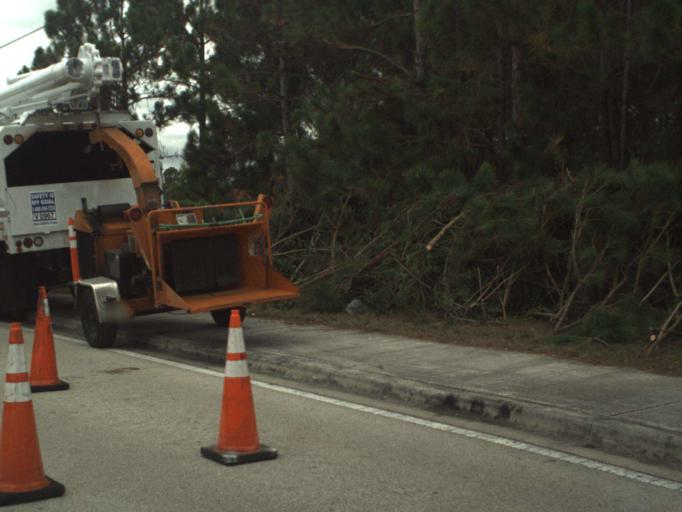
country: US
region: Florida
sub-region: Saint Lucie County
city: Port Saint Lucie
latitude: 27.3000
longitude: -80.3497
